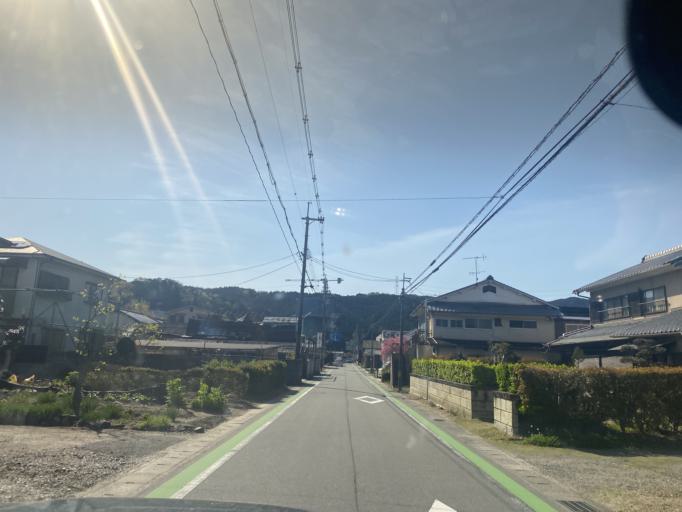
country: JP
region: Kyoto
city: Uji
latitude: 34.8528
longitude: 135.8504
